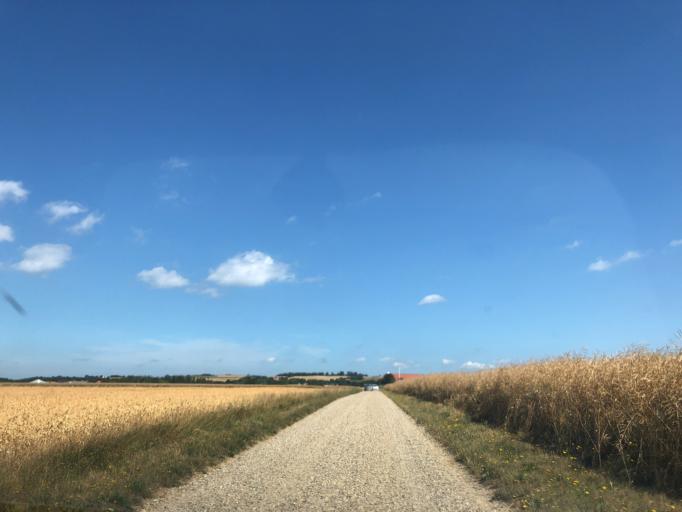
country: DK
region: North Denmark
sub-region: Morso Kommune
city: Nykobing Mors
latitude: 56.8096
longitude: 8.9924
